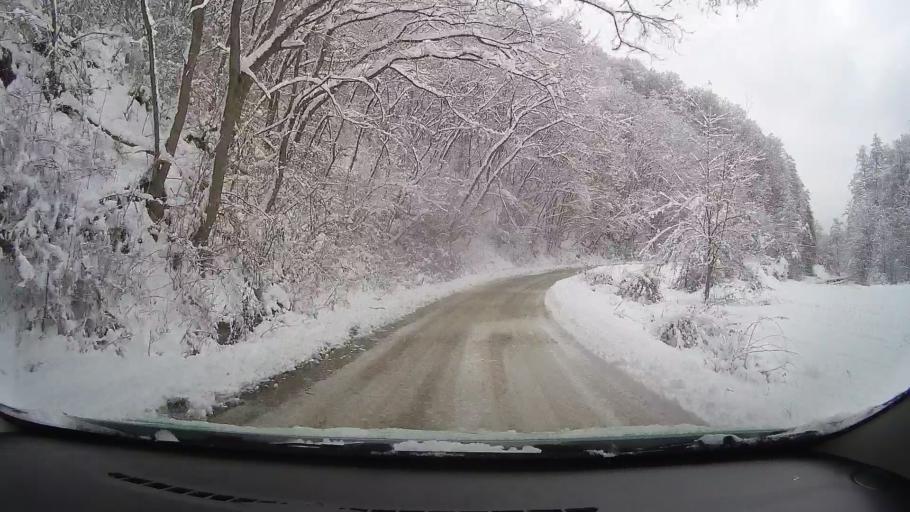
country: RO
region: Alba
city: Pianu de Sus
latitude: 45.8705
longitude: 23.4943
